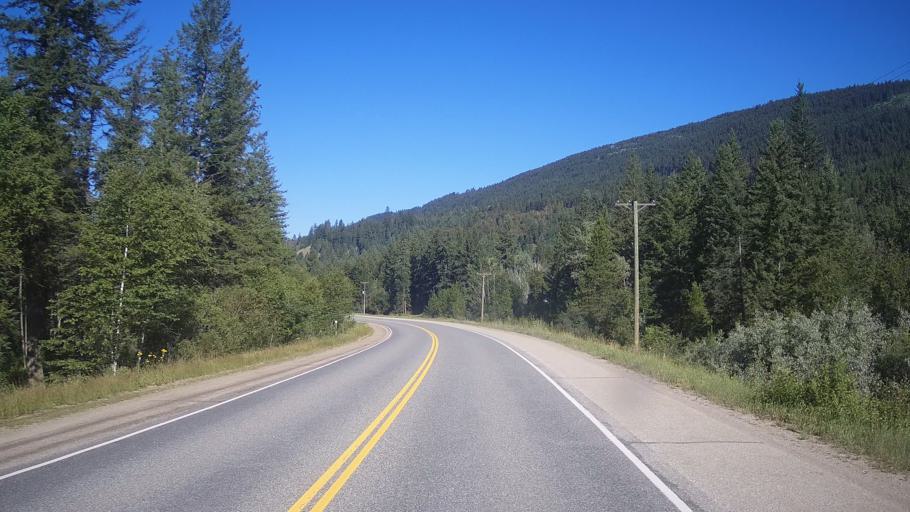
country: CA
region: British Columbia
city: Chase
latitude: 51.5853
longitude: -119.8218
